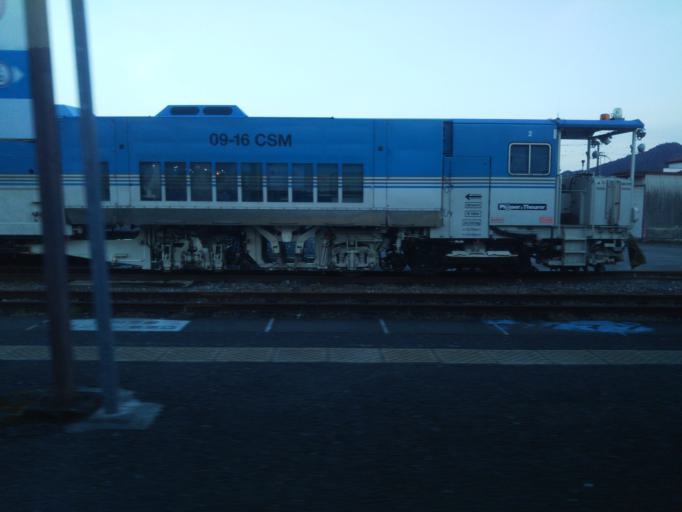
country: JP
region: Kochi
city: Susaki
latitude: 33.3289
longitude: 133.2265
